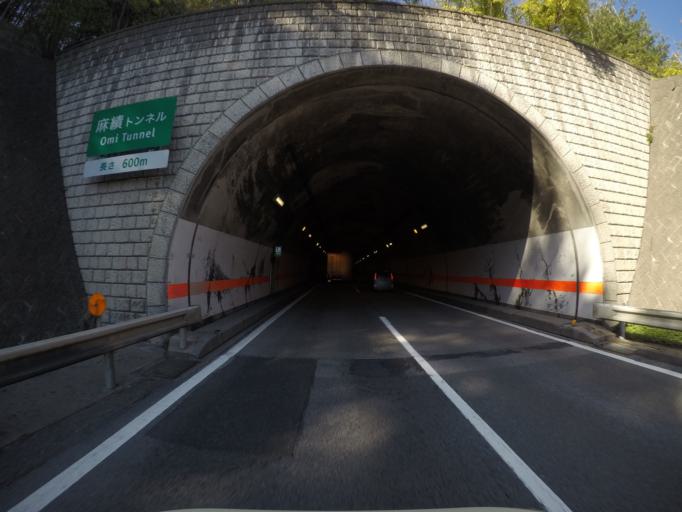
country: JP
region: Nagano
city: Omachi
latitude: 36.4568
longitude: 138.0610
